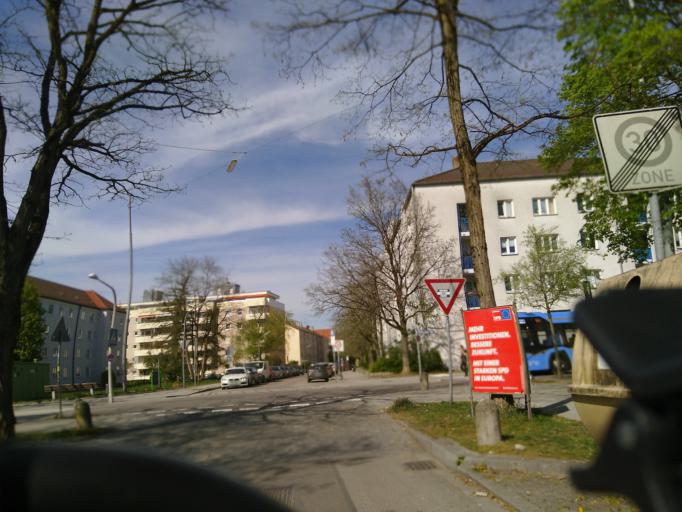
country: DE
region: Bavaria
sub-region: Upper Bavaria
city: Munich
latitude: 48.1096
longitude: 11.5887
